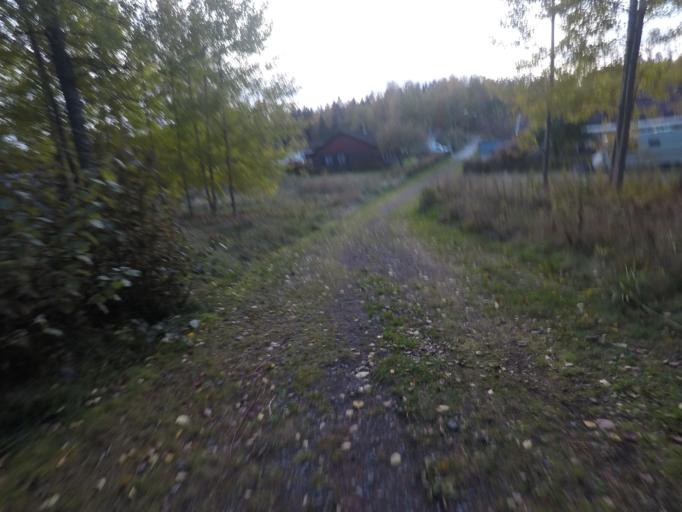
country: SE
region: OErebro
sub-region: Karlskoga Kommun
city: Karlskoga
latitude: 59.3096
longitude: 14.4722
